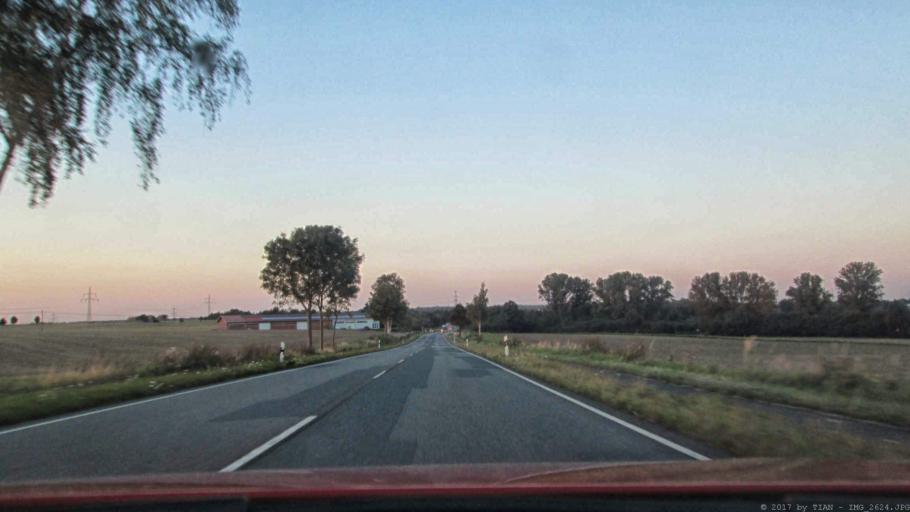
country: DE
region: Lower Saxony
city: Lehre
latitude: 52.3499
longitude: 10.6910
